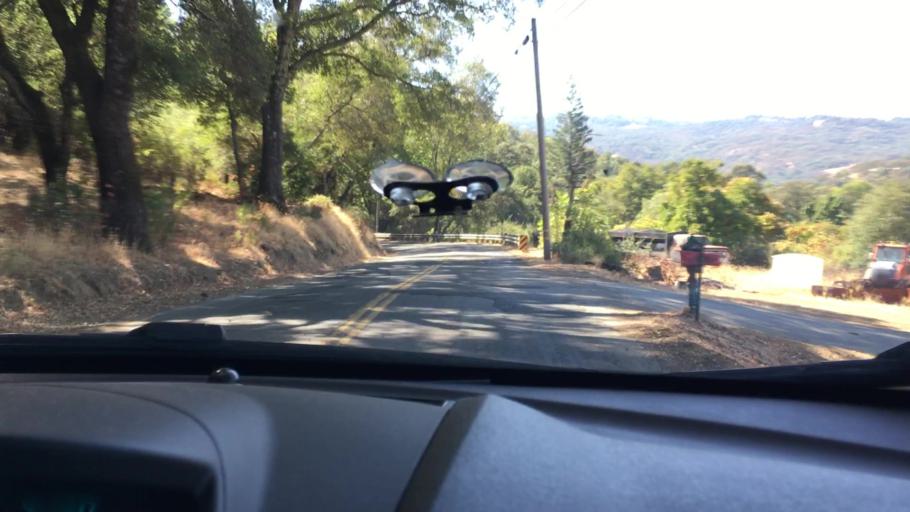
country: US
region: California
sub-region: Solano County
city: Green Valley
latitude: 38.3341
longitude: -122.1271
